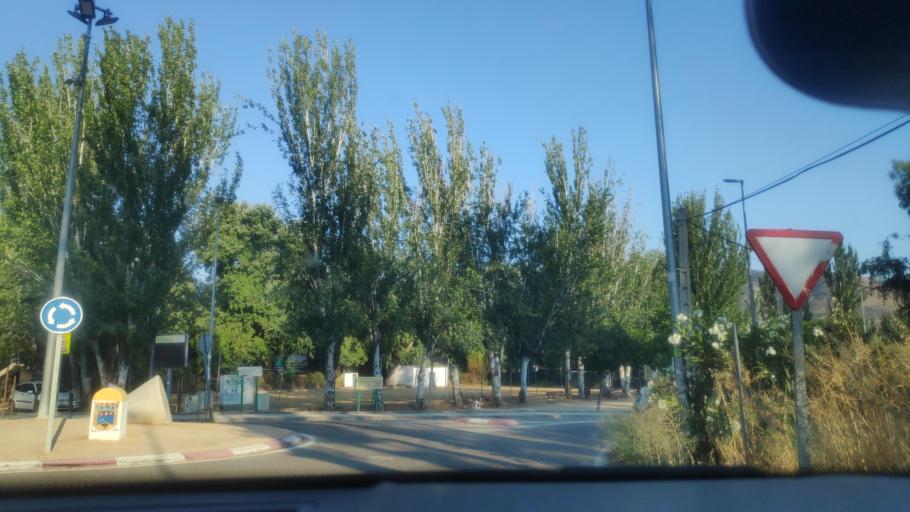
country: ES
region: Andalusia
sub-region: Provincia de Jaen
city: Jaen
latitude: 37.7202
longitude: -3.7636
